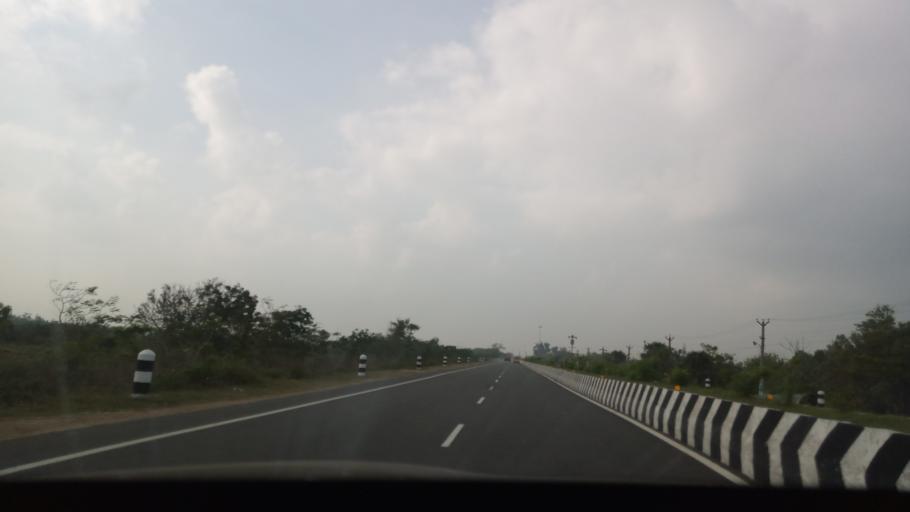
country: IN
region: Tamil Nadu
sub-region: Kancheepuram
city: Injambakkam
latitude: 12.7686
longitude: 80.2475
